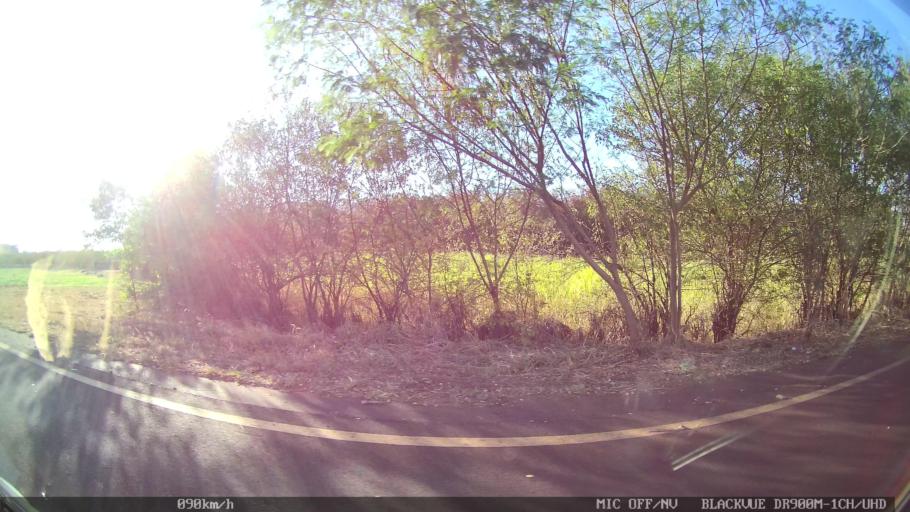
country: BR
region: Sao Paulo
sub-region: Guapiacu
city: Guapiacu
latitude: -20.7720
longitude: -49.2223
